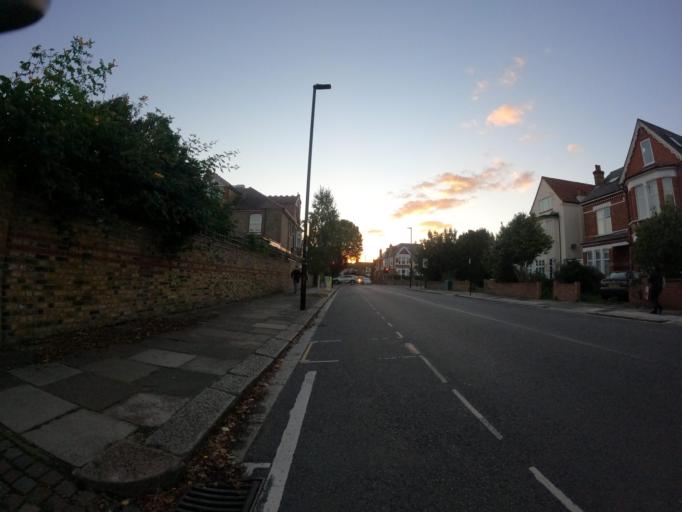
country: GB
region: England
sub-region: Greater London
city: Acton
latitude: 51.5133
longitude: -0.2814
